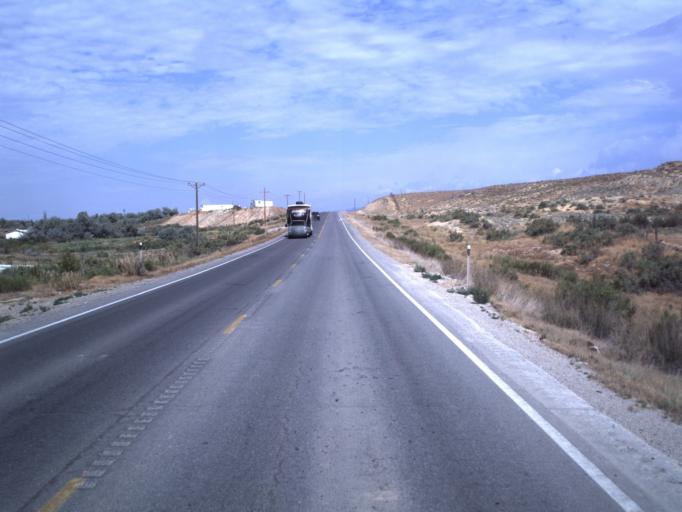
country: US
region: Utah
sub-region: Uintah County
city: Naples
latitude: 40.3934
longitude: -109.4504
